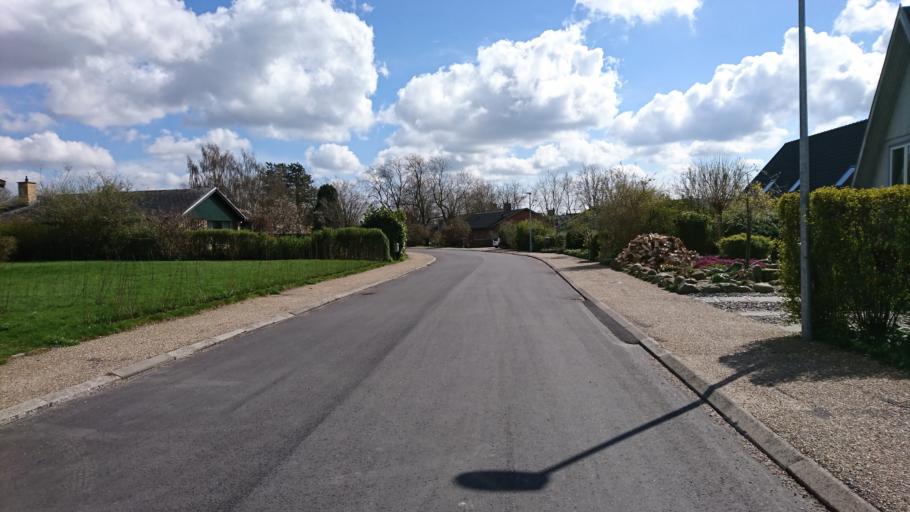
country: DK
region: Capital Region
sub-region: Egedal Kommune
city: Ganlose
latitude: 55.7919
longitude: 12.2611
